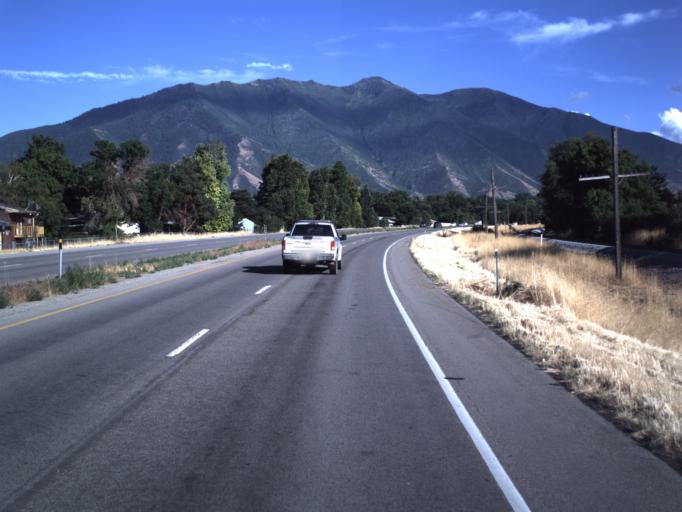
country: US
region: Utah
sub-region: Utah County
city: Springville
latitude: 40.1536
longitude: -111.6080
